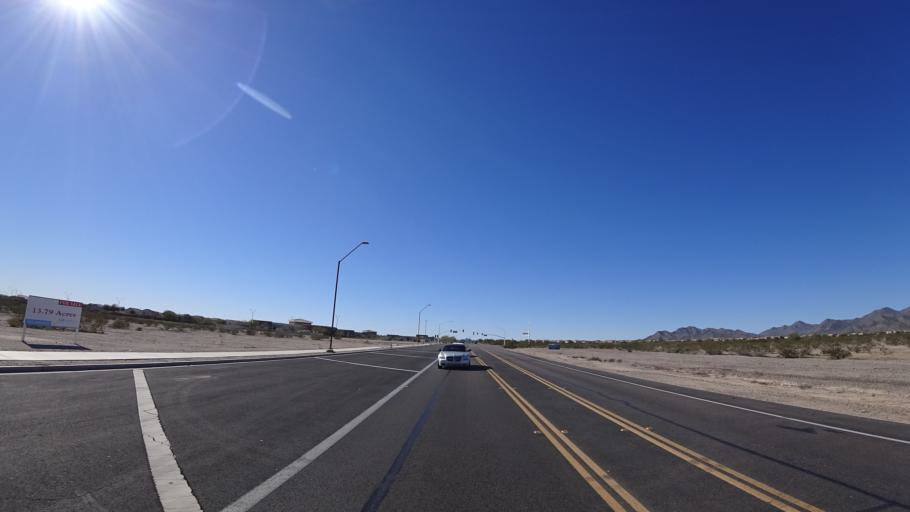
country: US
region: Arizona
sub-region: Maricopa County
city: Buckeye
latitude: 33.4356
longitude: -112.5139
